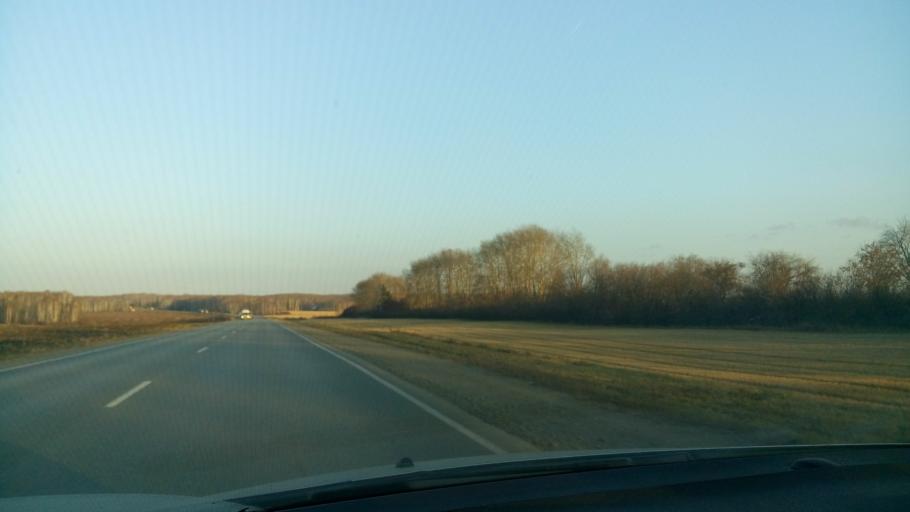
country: RU
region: Sverdlovsk
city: Yelanskiy
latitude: 56.7594
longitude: 62.3821
